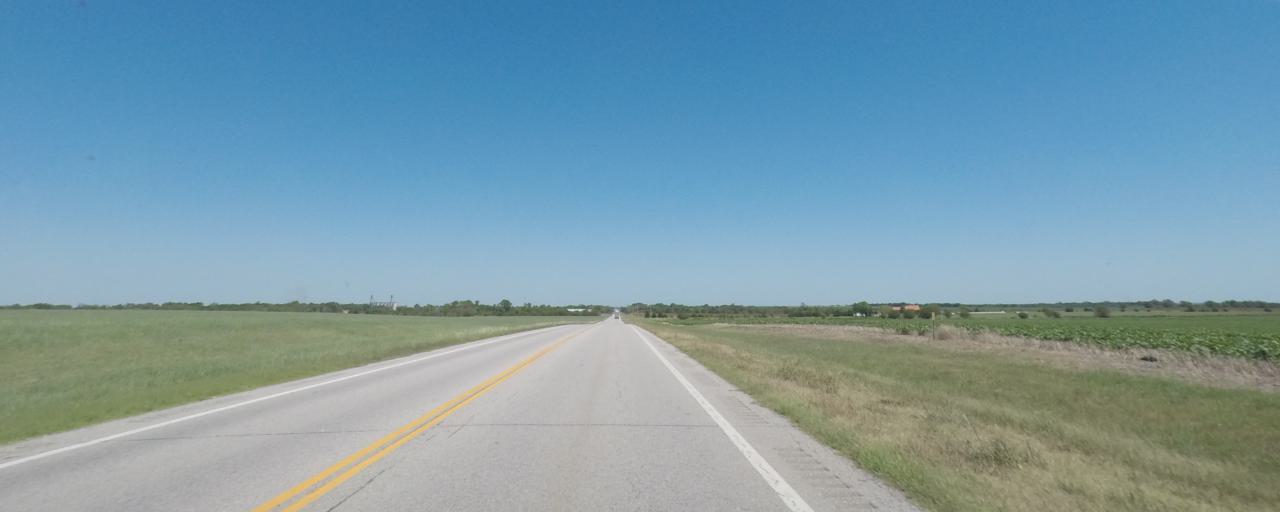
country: US
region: Kansas
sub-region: Sumner County
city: Wellington
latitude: 37.3625
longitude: -97.3850
